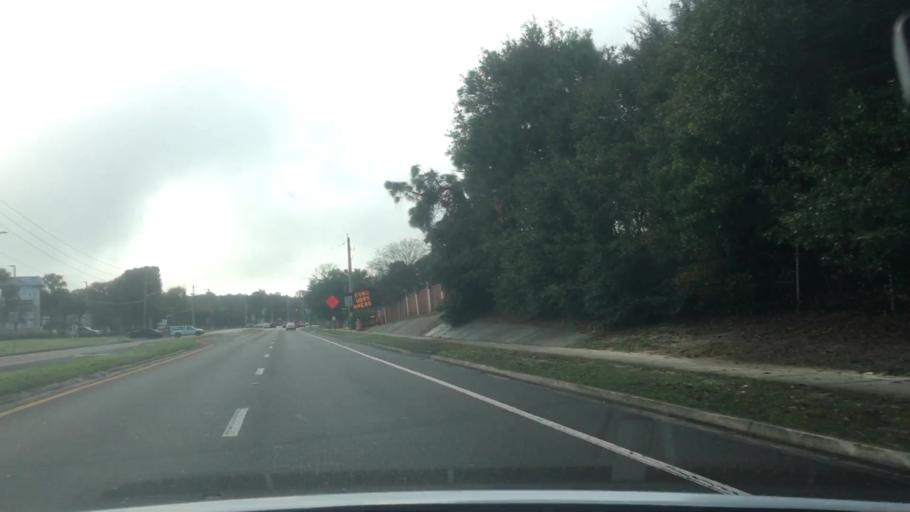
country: US
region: Florida
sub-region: Duval County
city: Atlantic Beach
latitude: 30.3633
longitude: -81.5029
